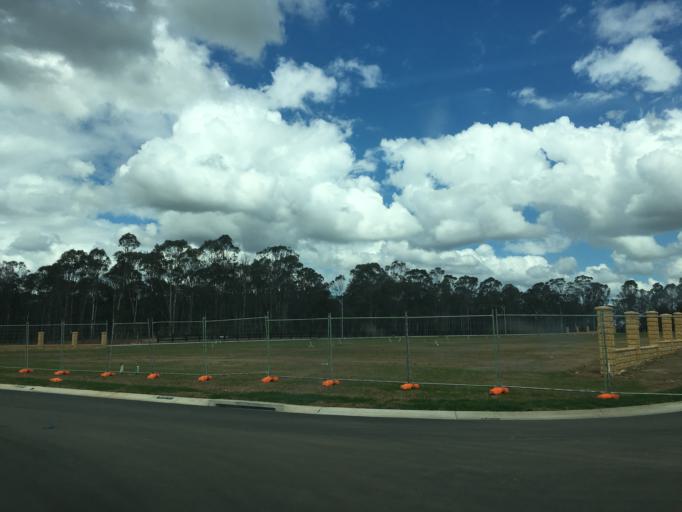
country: AU
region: New South Wales
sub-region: Campbelltown Municipality
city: Denham Court
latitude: -33.9902
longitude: 150.8010
